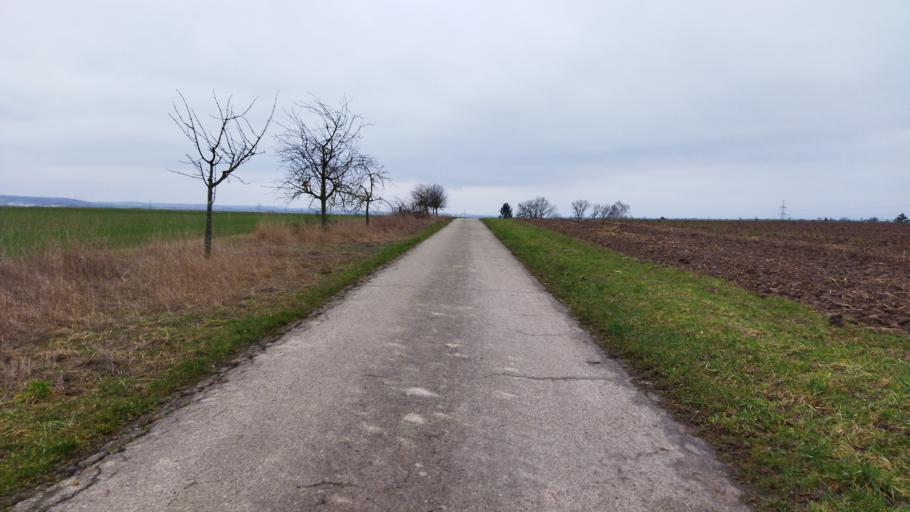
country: DE
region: Baden-Wuerttemberg
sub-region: Regierungsbezirk Stuttgart
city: Nordheim
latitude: 49.1244
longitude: 9.1573
